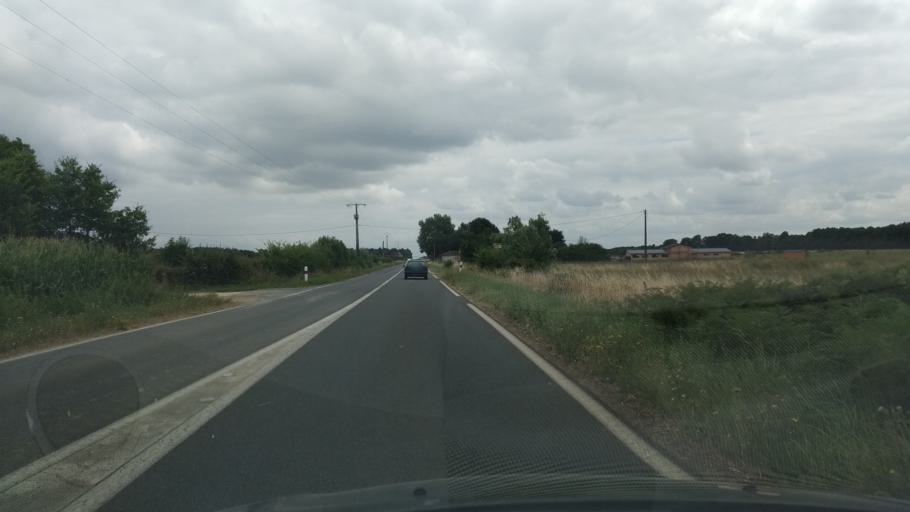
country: FR
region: Poitou-Charentes
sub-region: Departement de la Vienne
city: Saint-Maurice-la-Clouere
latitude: 46.4132
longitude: 0.3868
